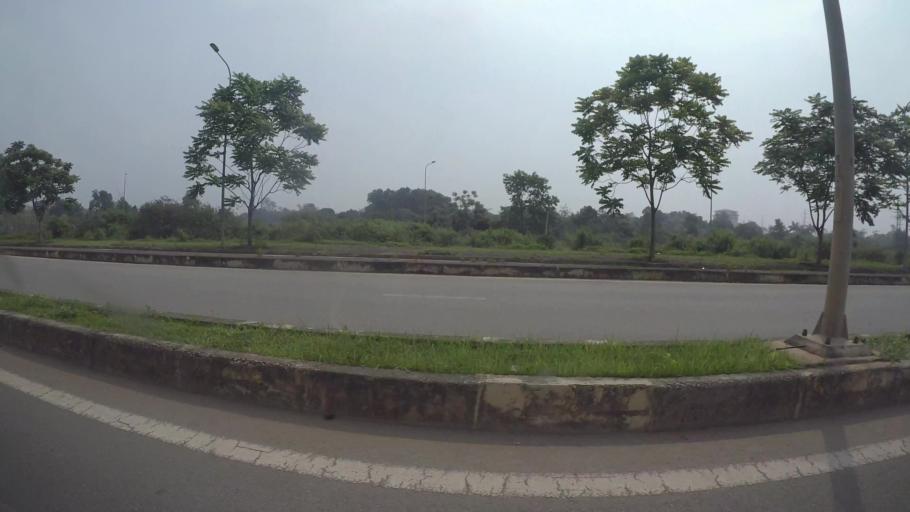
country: VN
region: Ha Noi
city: Lien Quan
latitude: 20.9925
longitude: 105.5358
